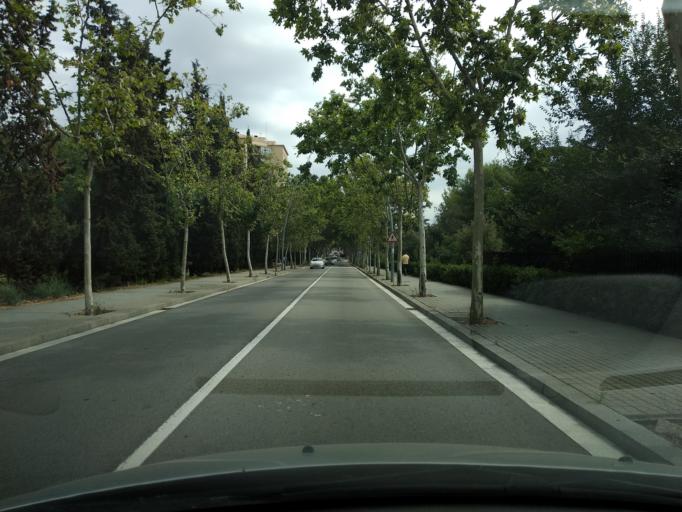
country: ES
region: Catalonia
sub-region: Provincia de Barcelona
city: Granollers
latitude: 41.6020
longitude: 2.2804
